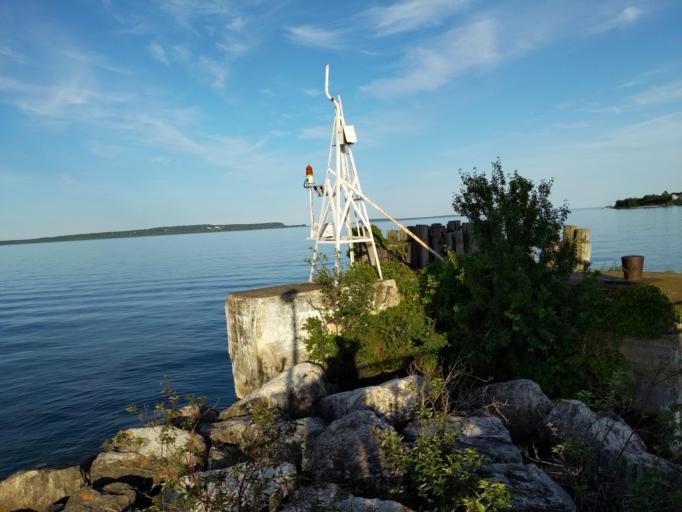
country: US
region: Michigan
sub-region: Mackinac County
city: Saint Ignace
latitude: 45.8660
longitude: -84.7154
